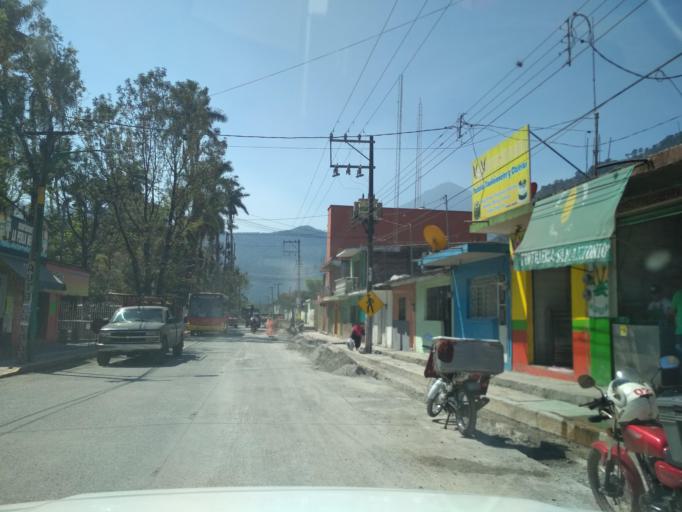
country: MX
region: Veracruz
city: Jalapilla
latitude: 18.8236
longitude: -97.0897
